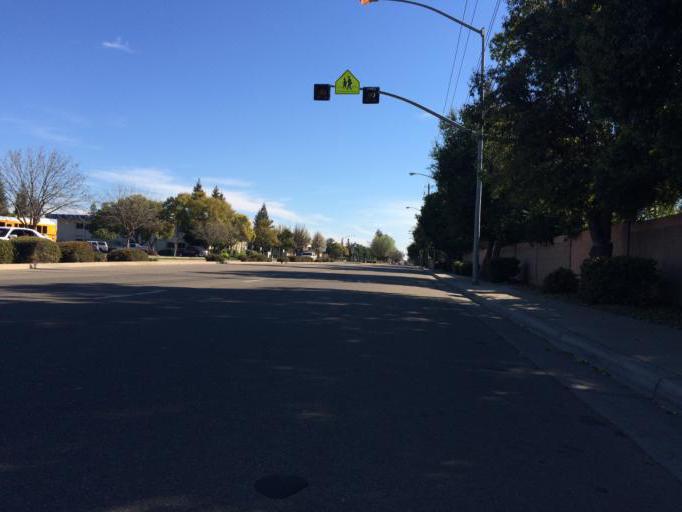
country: US
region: California
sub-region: Fresno County
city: Clovis
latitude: 36.8193
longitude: -119.6821
